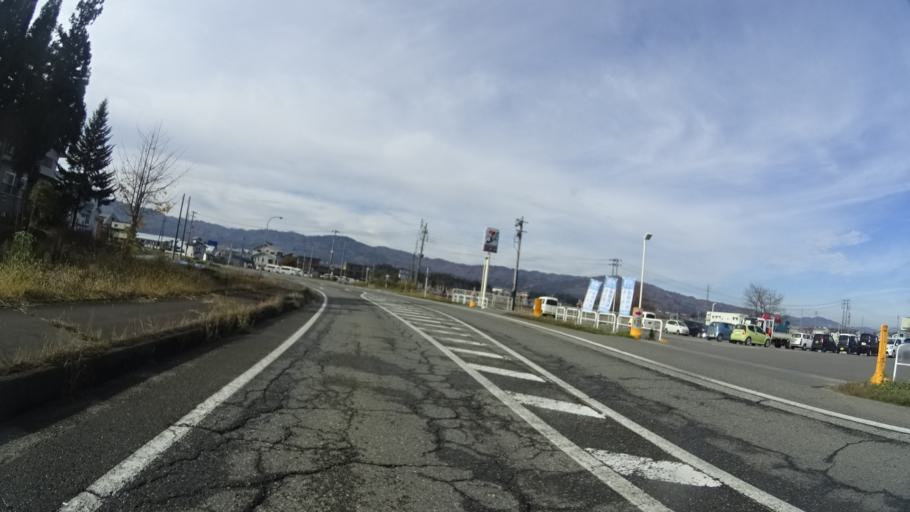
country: JP
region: Niigata
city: Muikamachi
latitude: 37.0835
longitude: 138.9011
